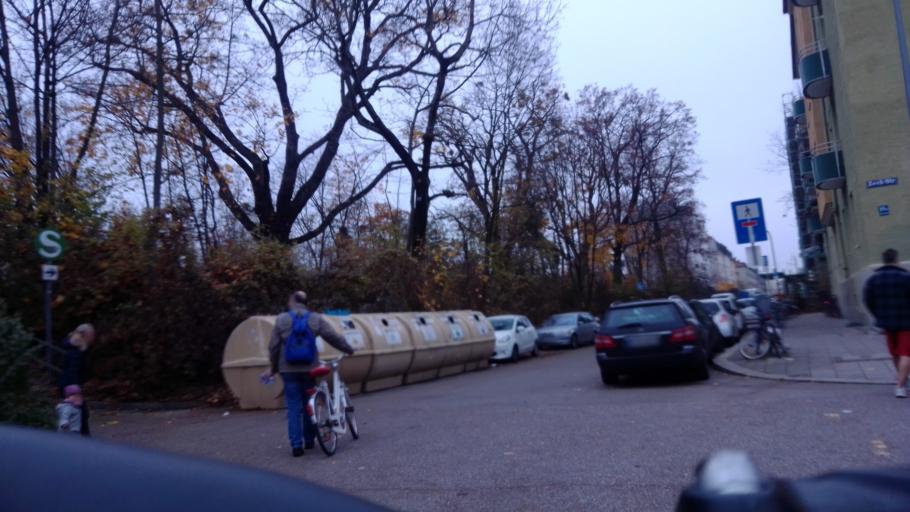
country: DE
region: Bavaria
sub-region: Upper Bavaria
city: Pullach im Isartal
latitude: 48.1070
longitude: 11.5373
